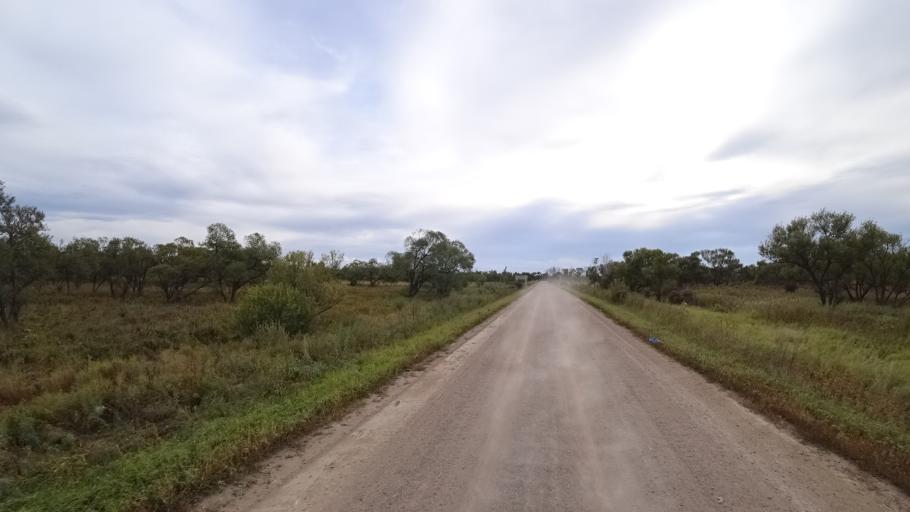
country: RU
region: Amur
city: Arkhara
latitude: 49.3760
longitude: 130.2090
